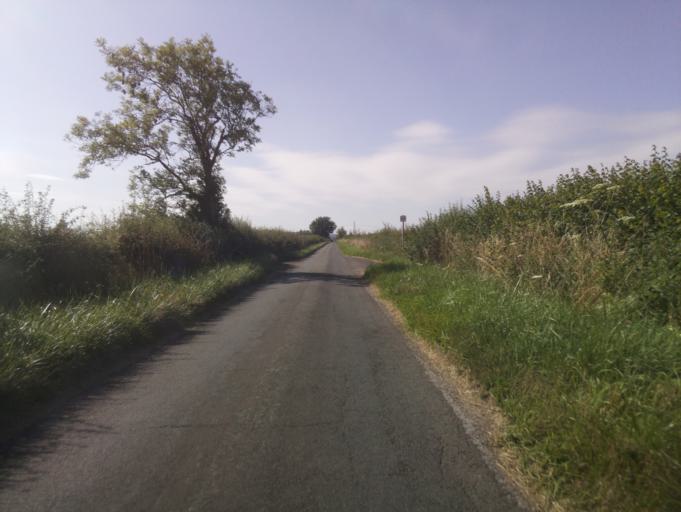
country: GB
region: England
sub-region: Oxfordshire
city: Ducklington
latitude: 51.7175
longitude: -1.4943
